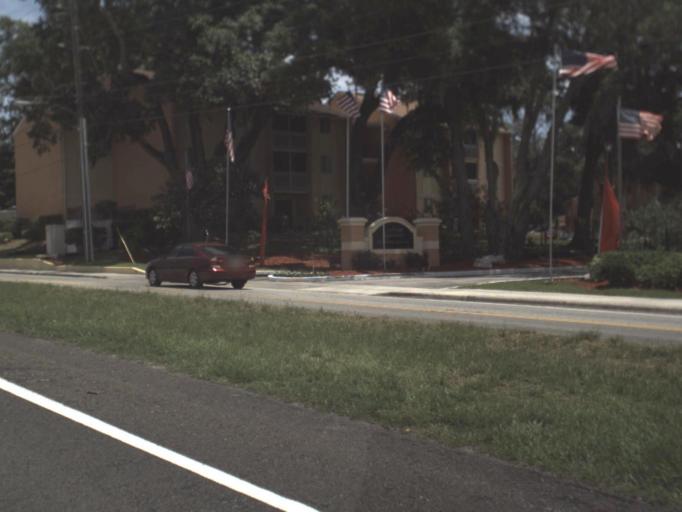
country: US
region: Florida
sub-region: Duval County
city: Jacksonville
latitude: 30.3275
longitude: -81.5807
